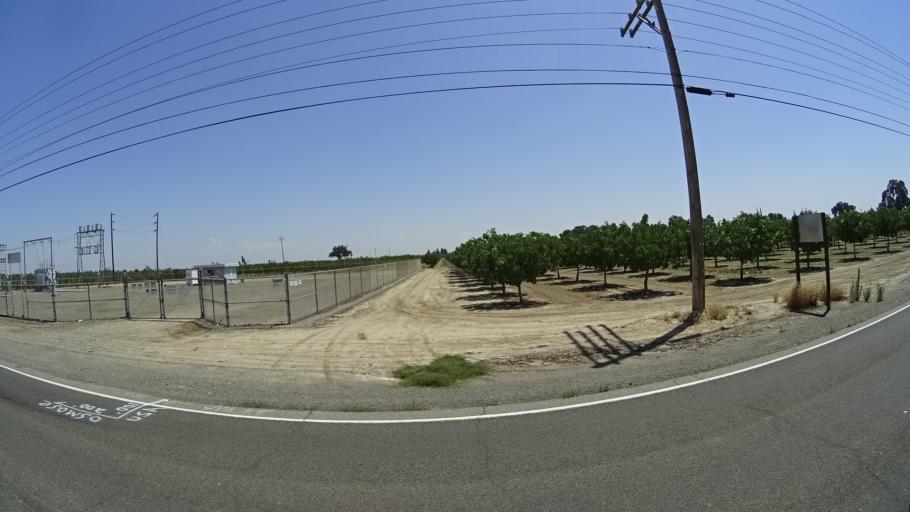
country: US
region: California
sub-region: Fresno County
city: Laton
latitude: 36.4040
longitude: -119.6863
